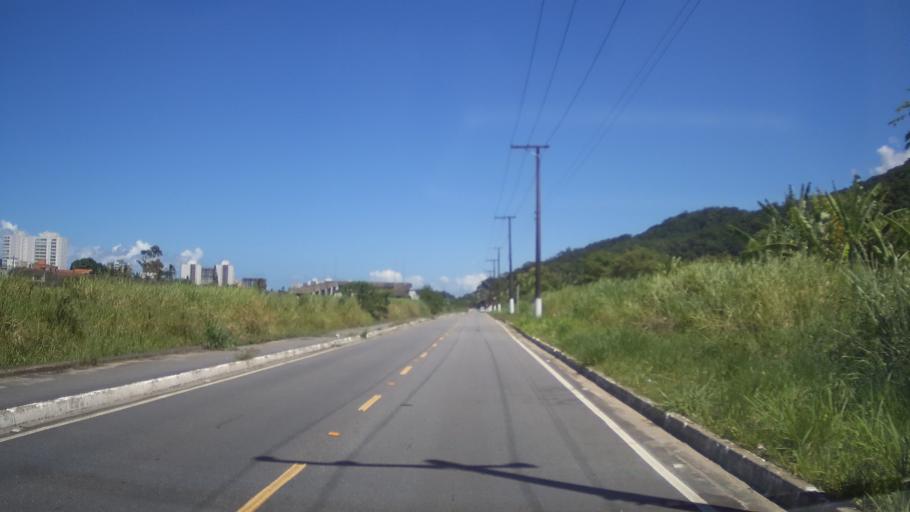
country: BR
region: Sao Paulo
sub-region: Mongagua
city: Mongagua
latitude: -24.0821
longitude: -46.6012
